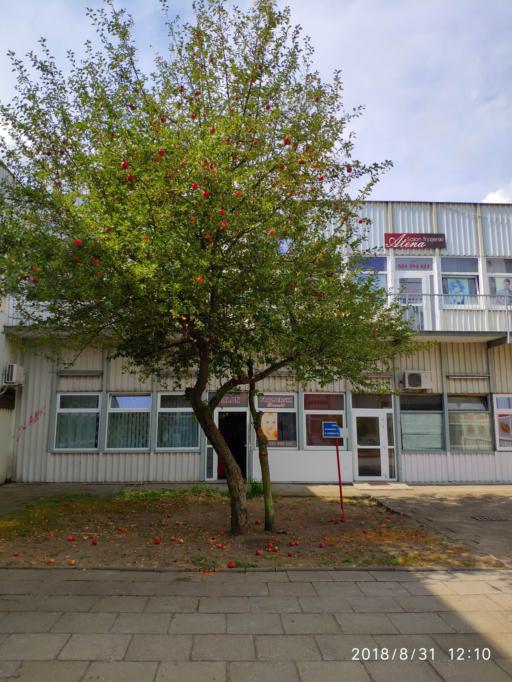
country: PL
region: Lubusz
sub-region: Zielona Gora
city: Zielona Gora
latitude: 51.9379
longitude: 15.4843
